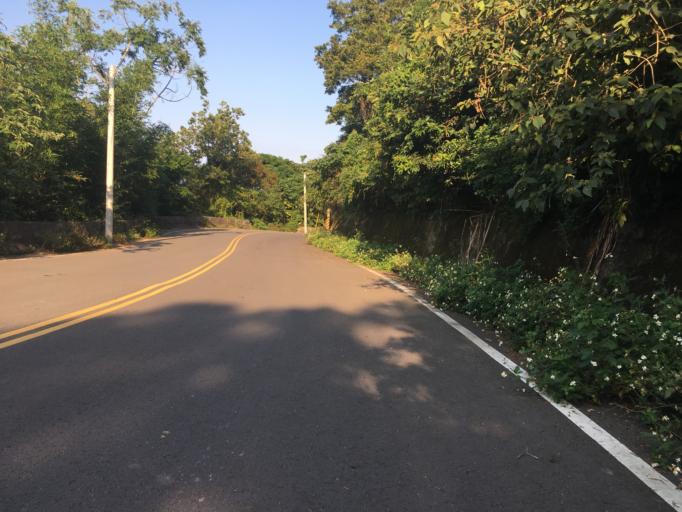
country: TW
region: Taiwan
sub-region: Hsinchu
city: Hsinchu
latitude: 24.7327
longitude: 120.9879
